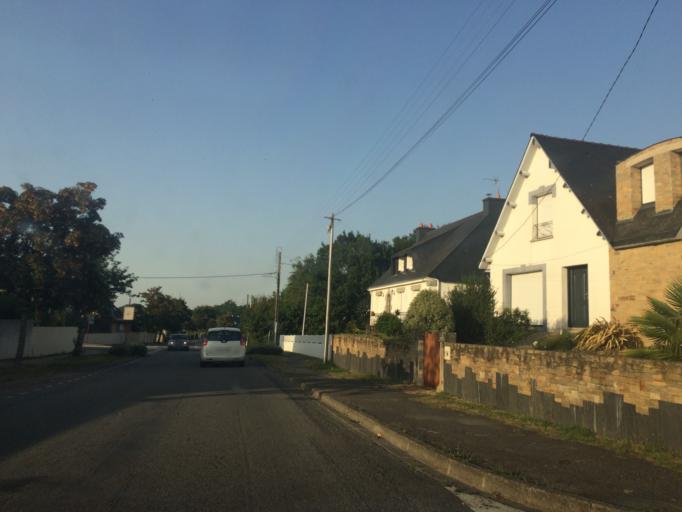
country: FR
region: Brittany
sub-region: Departement du Morbihan
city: Muzillac
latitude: 47.5571
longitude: -2.4780
